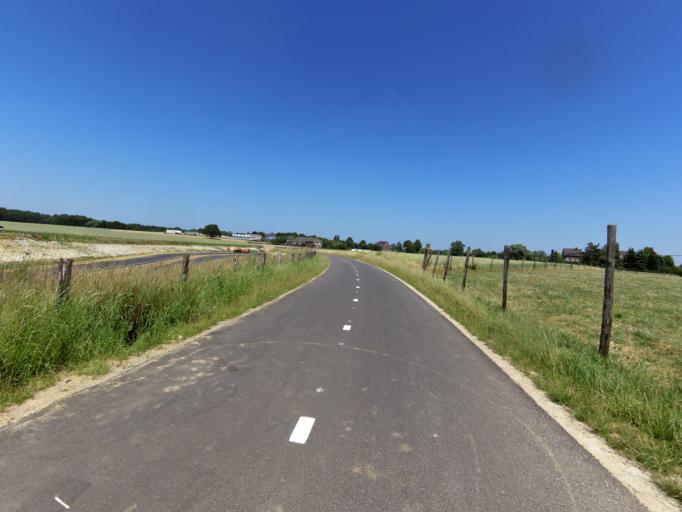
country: NL
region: Limburg
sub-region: Gemeente Simpelveld
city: Simpelveld
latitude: 50.8436
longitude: 6.0176
